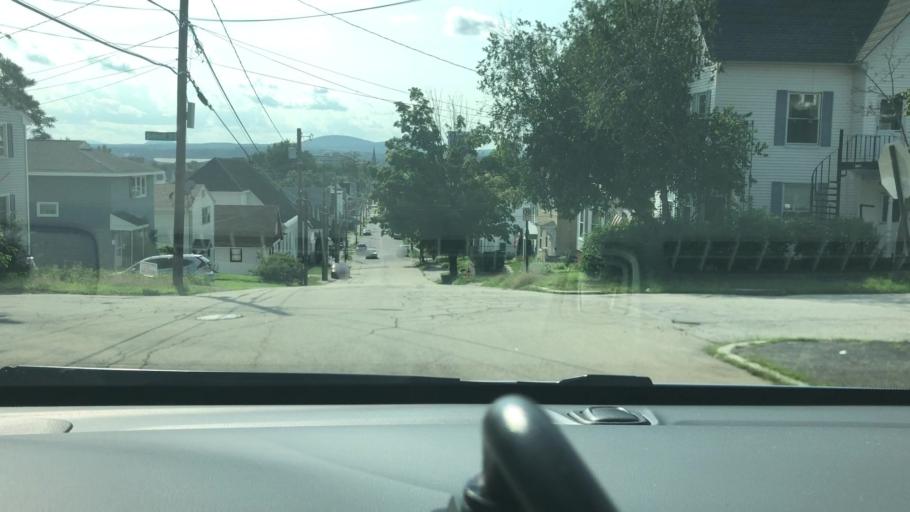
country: US
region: New Hampshire
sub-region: Hillsborough County
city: Manchester
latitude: 42.9894
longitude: -71.4448
